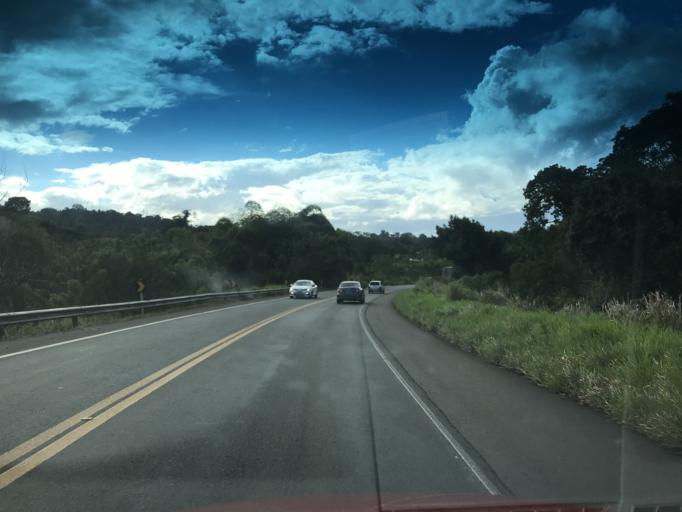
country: BR
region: Bahia
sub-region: Ibirapitanga
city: Ibirapitanga
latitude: -14.1696
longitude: -39.3273
